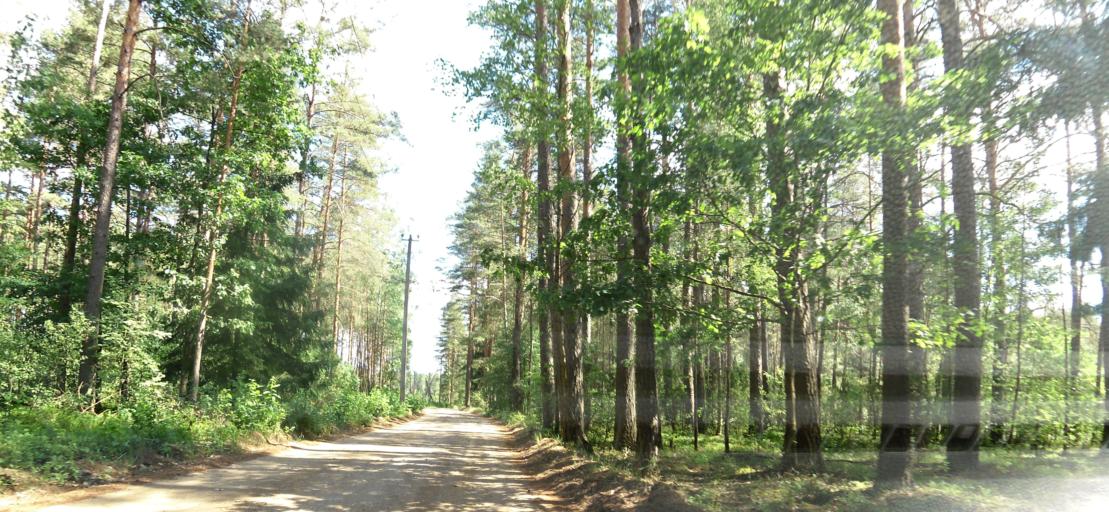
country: LT
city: Nemencine
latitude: 54.8228
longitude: 25.4083
